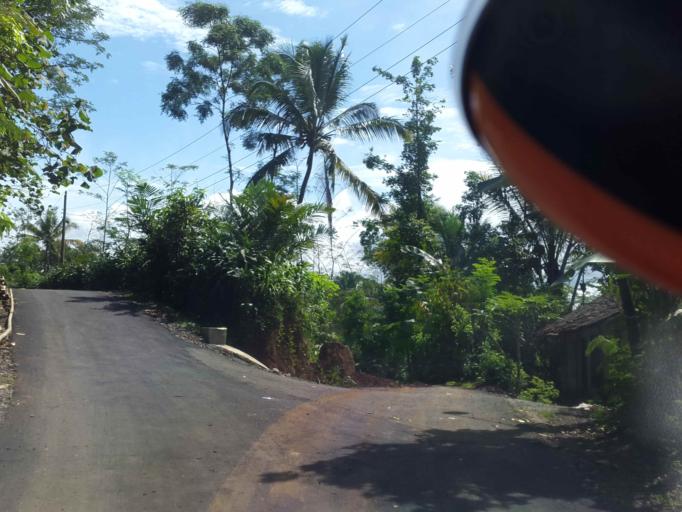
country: ID
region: Central Java
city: Wonosobo
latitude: -7.3518
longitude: 109.6968
